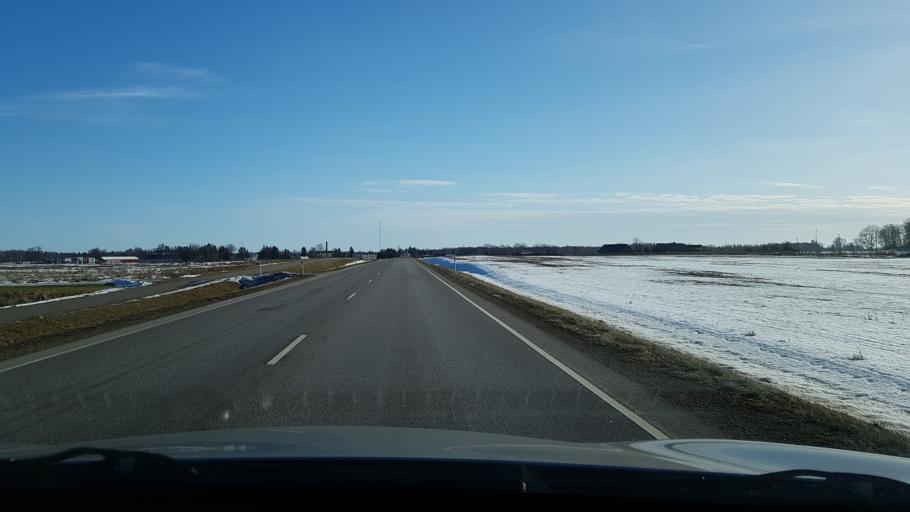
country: EE
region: Viljandimaa
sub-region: Vohma linn
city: Vohma
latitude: 58.6330
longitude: 25.7097
